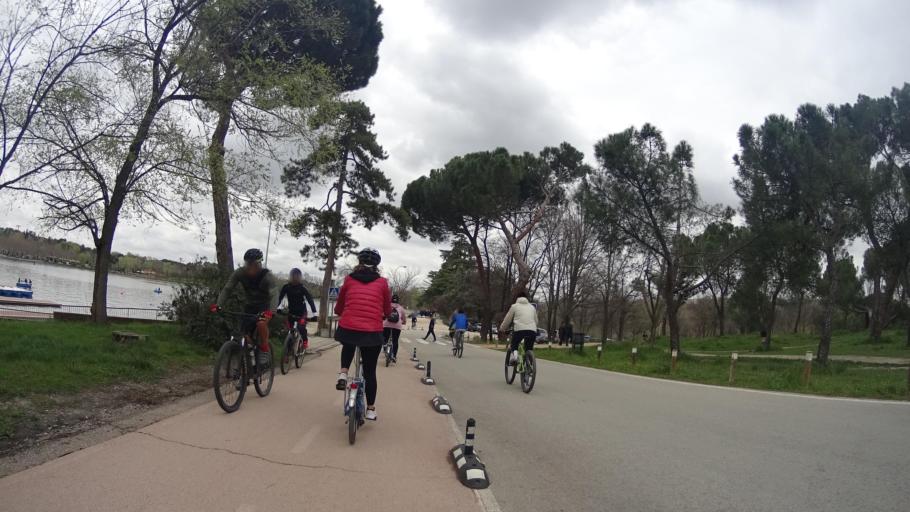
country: ES
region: Madrid
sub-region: Provincia de Madrid
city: Moncloa-Aravaca
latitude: 40.4172
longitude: -3.7310
